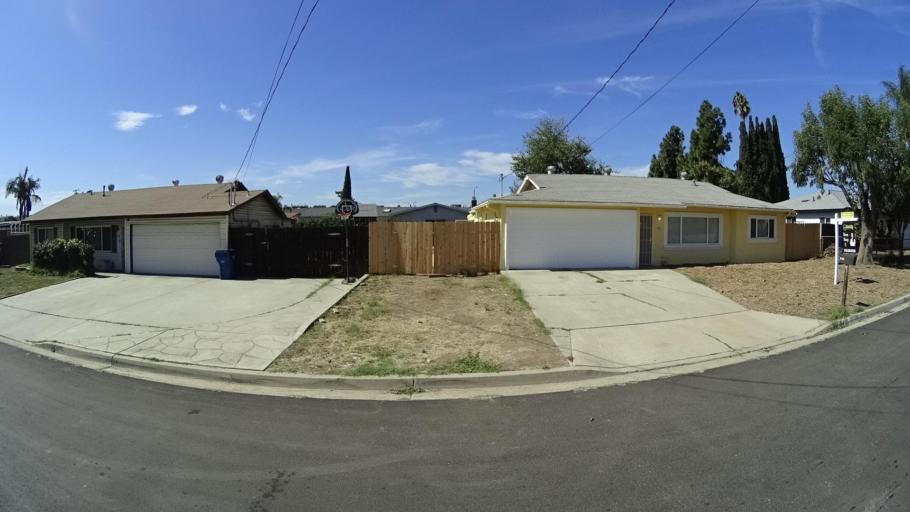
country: US
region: California
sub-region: San Diego County
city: La Presa
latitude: 32.7129
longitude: -117.0092
